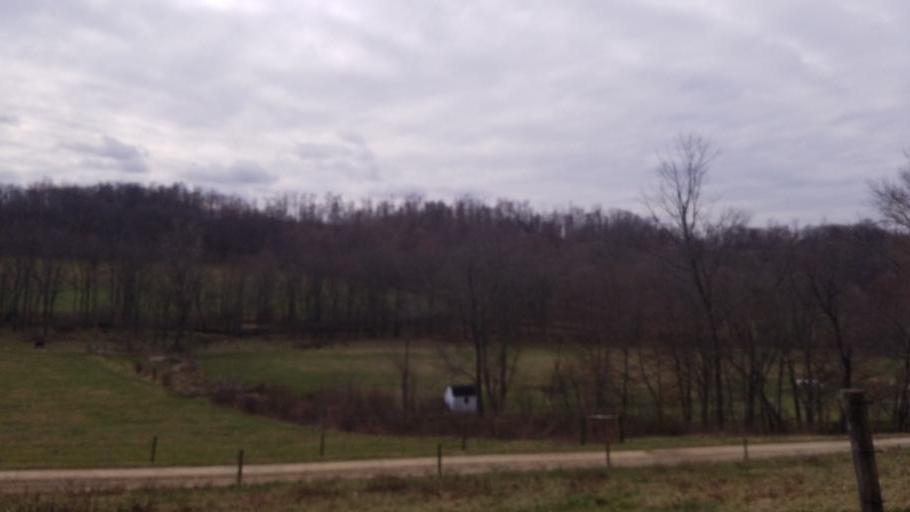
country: US
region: Ohio
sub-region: Sandusky County
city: Bellville
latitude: 40.5576
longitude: -82.3826
